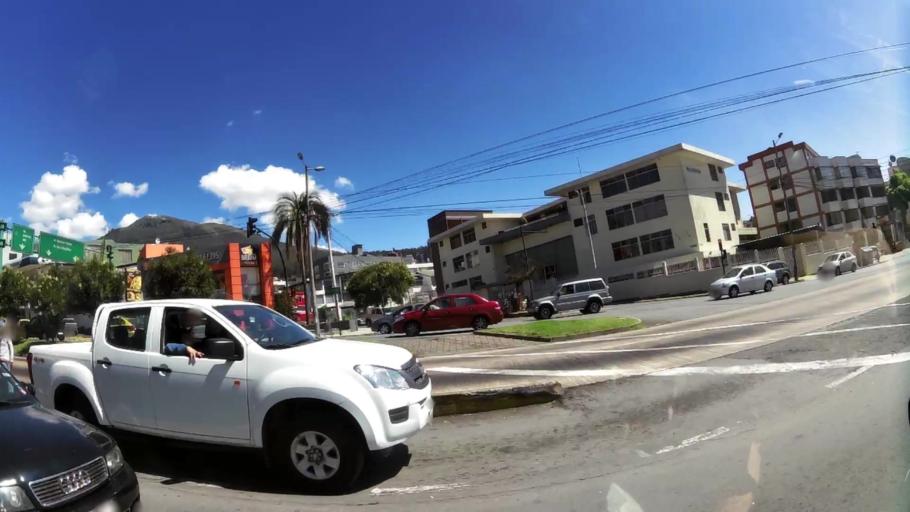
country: EC
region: Pichincha
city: Quito
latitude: -0.1723
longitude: -78.4913
